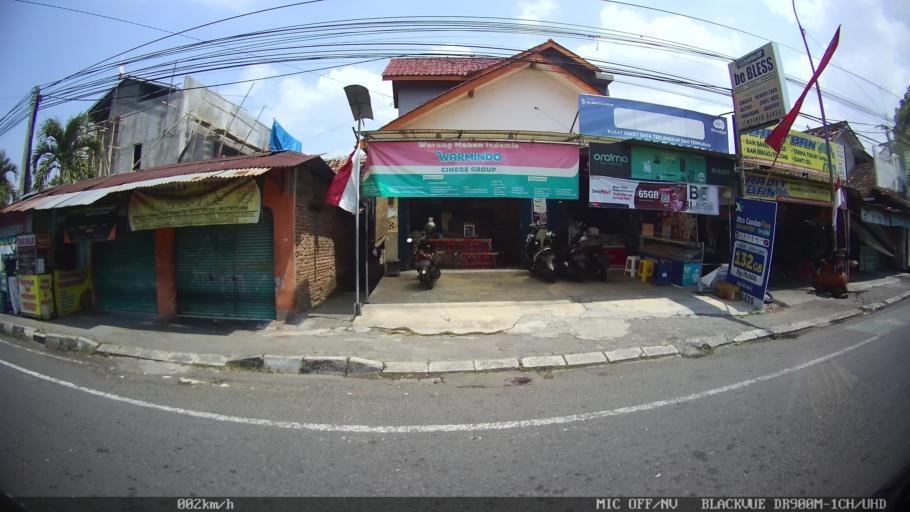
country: ID
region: Daerah Istimewa Yogyakarta
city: Yogyakarta
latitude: -7.8111
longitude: 110.4021
